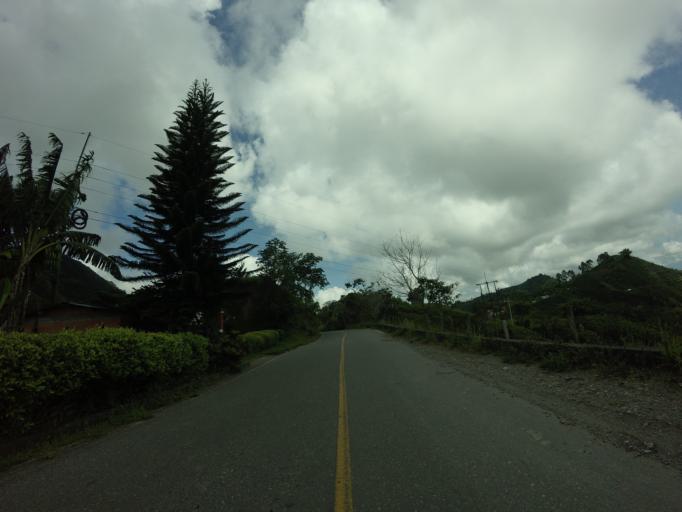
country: CO
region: Caldas
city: Marquetalia
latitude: 5.2998
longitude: -75.0277
